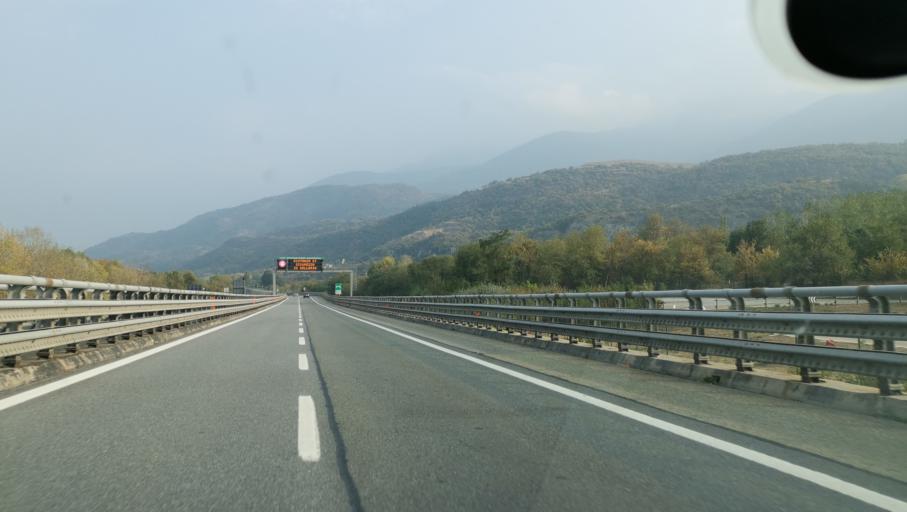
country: IT
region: Piedmont
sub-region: Provincia di Torino
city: Mattie
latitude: 45.1350
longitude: 7.0945
